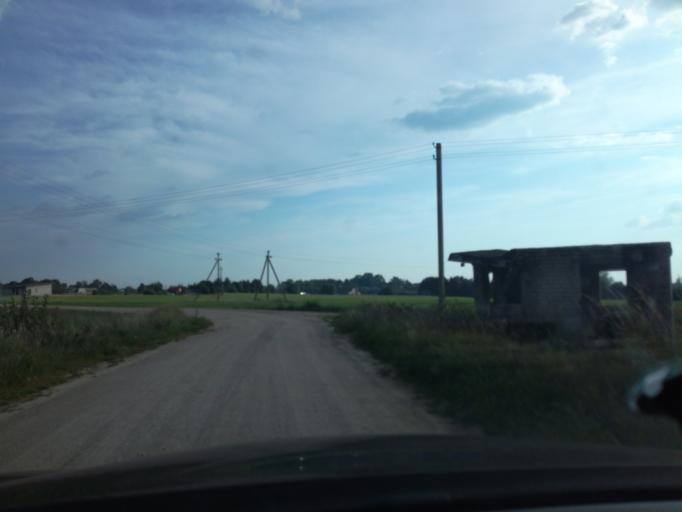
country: LT
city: Simnas
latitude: 54.3922
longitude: 23.8164
